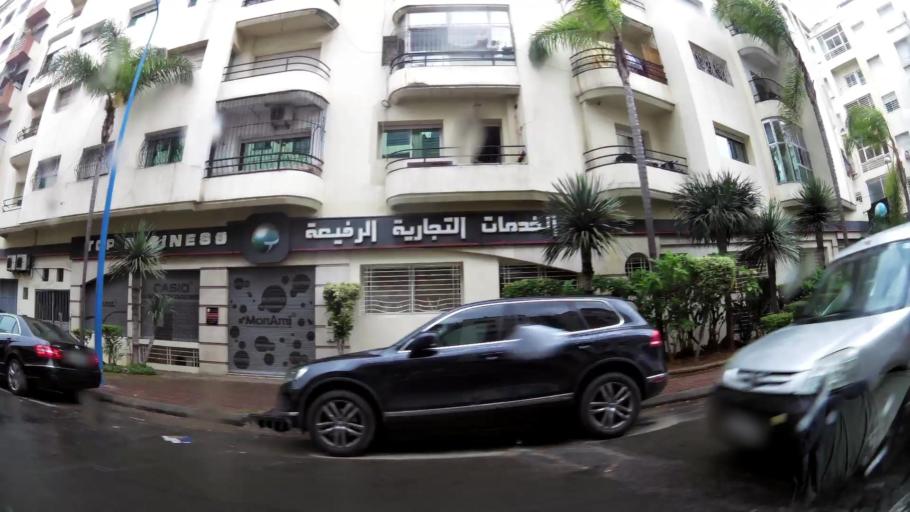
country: MA
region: Grand Casablanca
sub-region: Casablanca
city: Casablanca
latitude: 33.5724
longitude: -7.6125
